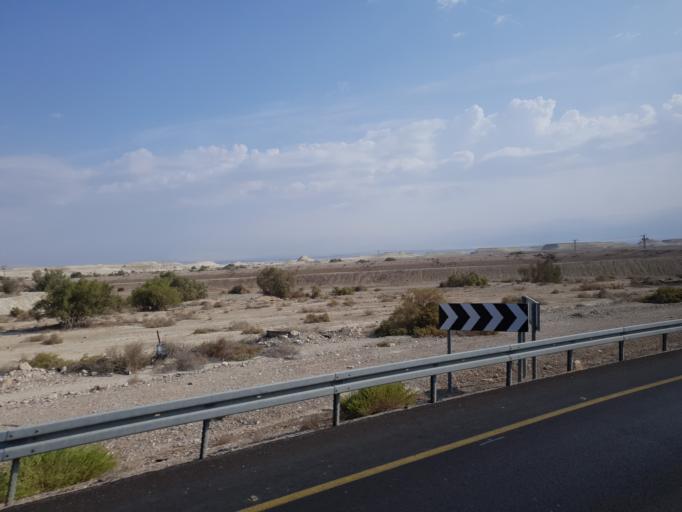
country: PS
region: West Bank
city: Jericho
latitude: 31.7964
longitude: 35.4952
